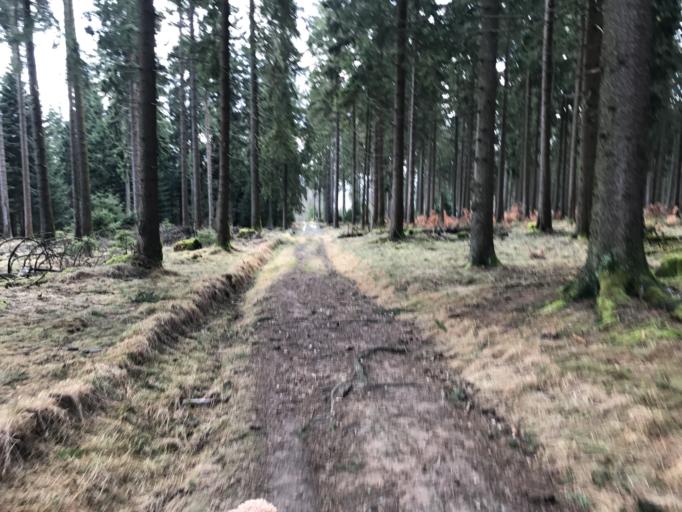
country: DE
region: Hesse
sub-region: Regierungsbezirk Darmstadt
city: Glashutten
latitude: 50.2154
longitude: 8.4431
